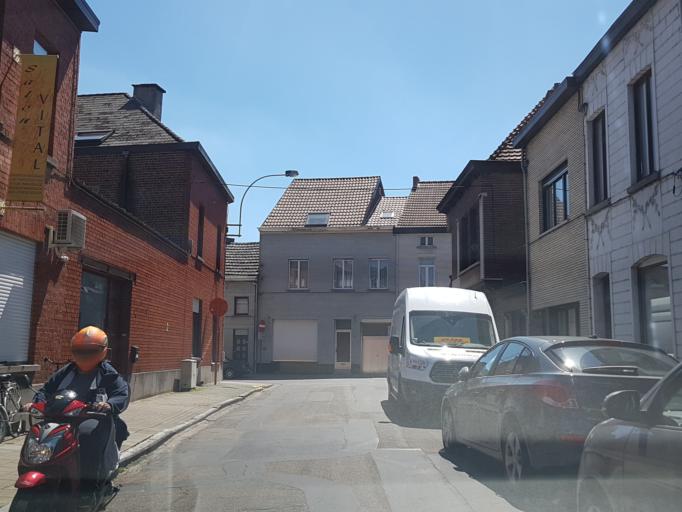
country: BE
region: Flanders
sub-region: Provincie Oost-Vlaanderen
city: Aalst
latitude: 50.9342
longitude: 4.0348
